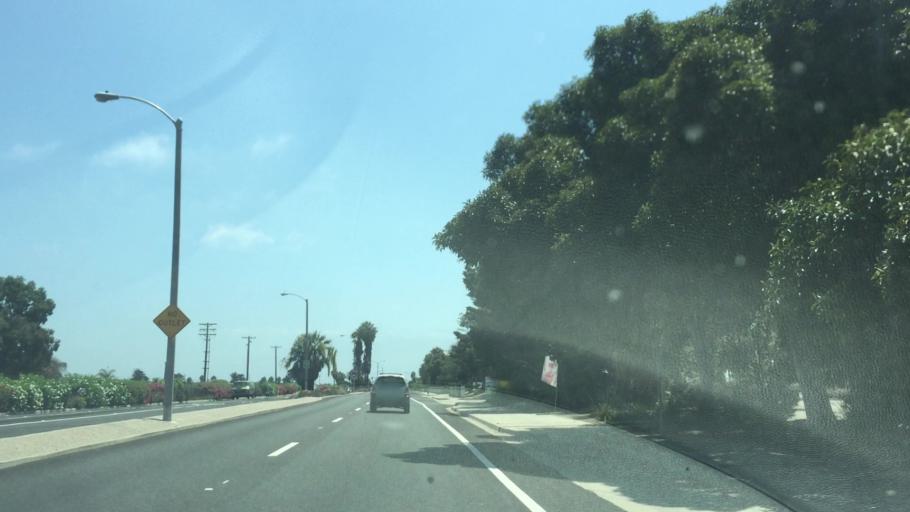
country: US
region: California
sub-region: Ventura County
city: Channel Islands Beach
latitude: 34.1755
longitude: -119.2216
